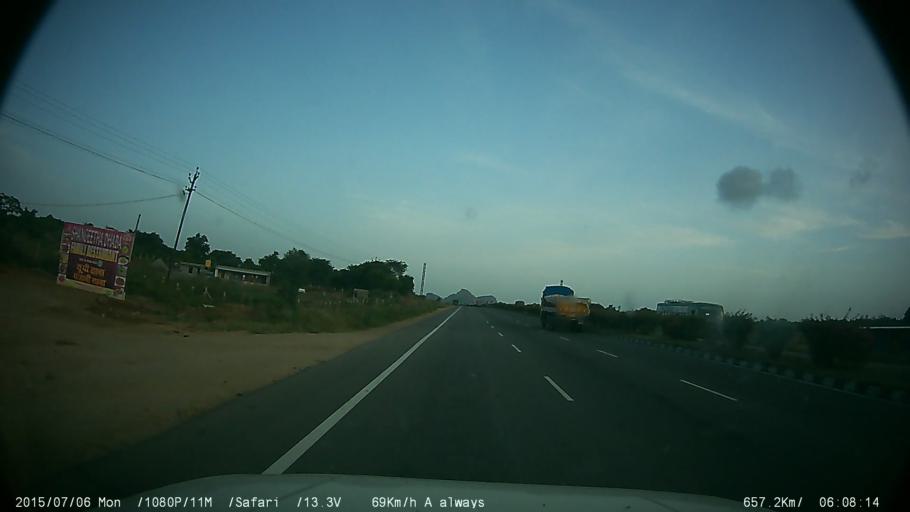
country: IN
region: Tamil Nadu
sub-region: Krishnagiri
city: Krishnagiri
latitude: 12.6423
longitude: 78.0569
